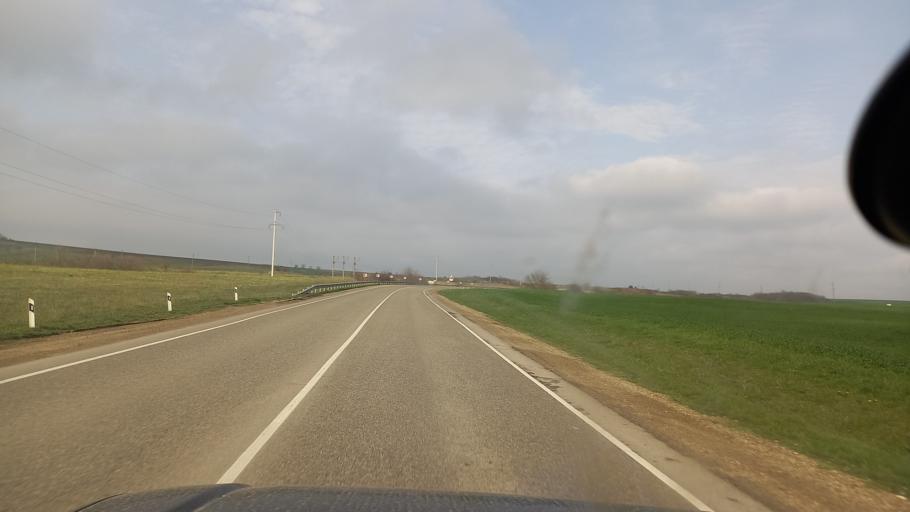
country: RU
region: Krasnodarskiy
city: Varenikovskaya
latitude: 45.0959
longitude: 37.5848
